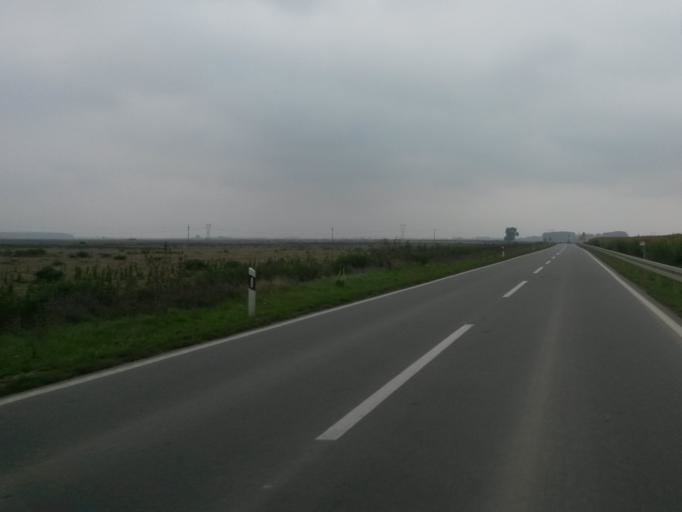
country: HR
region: Osjecko-Baranjska
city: Vladislavci
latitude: 45.4740
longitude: 18.5344
